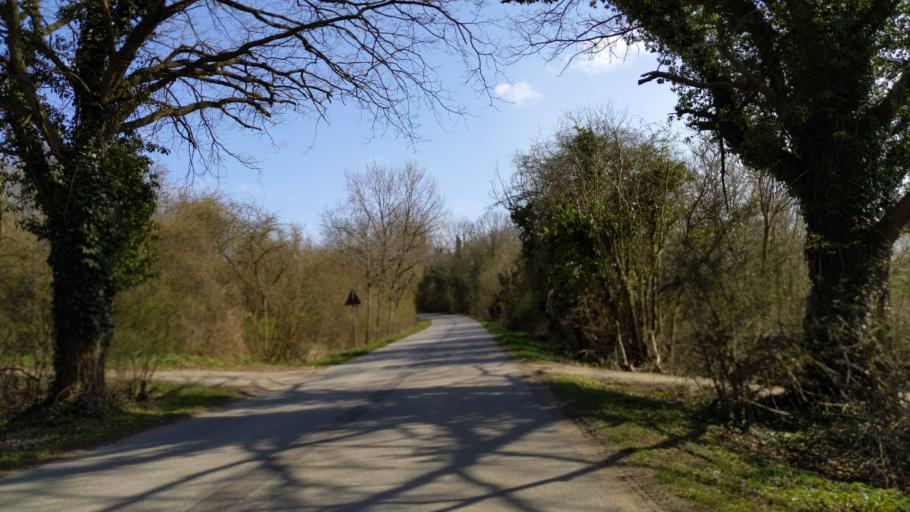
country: DE
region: Schleswig-Holstein
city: Schashagen
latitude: 54.1237
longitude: 10.8691
